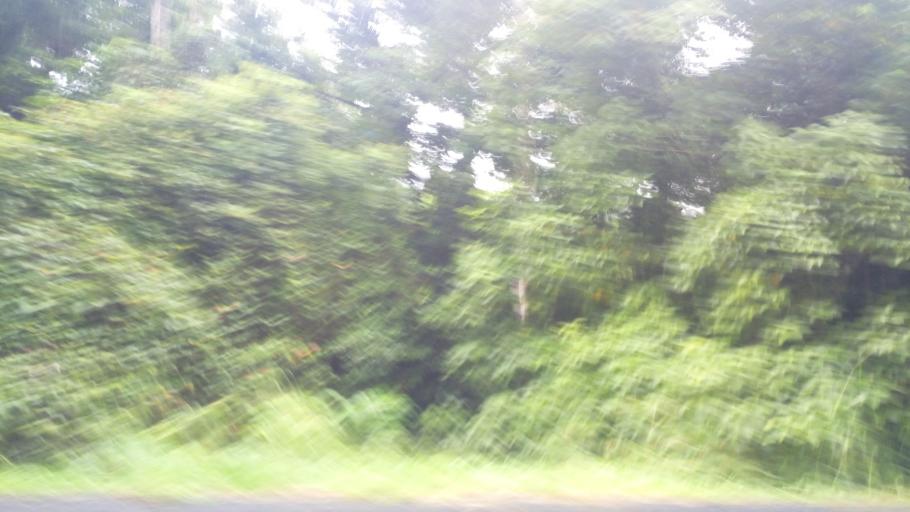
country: AU
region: Queensland
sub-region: Cassowary Coast
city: Innisfail
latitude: -17.6073
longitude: 145.7741
